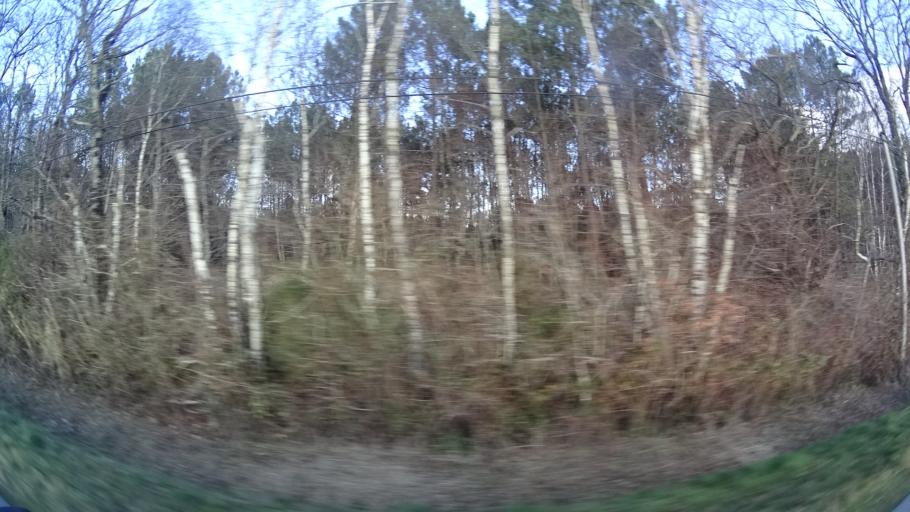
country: FR
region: Pays de la Loire
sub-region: Departement de la Loire-Atlantique
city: Fegreac
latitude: 47.5796
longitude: -1.9903
